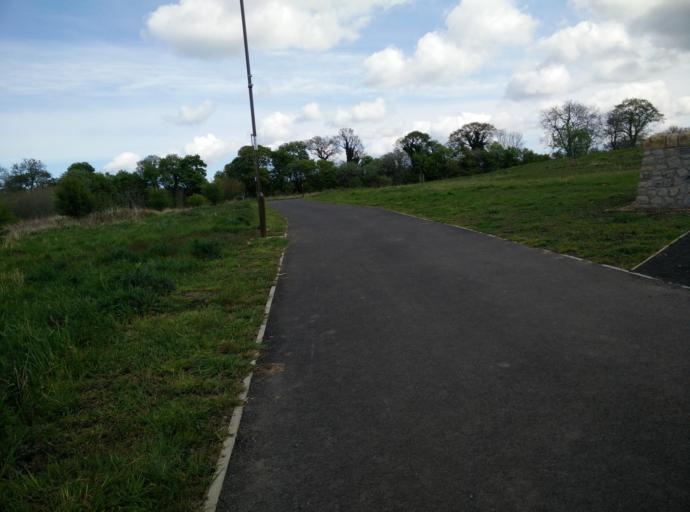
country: GB
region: Scotland
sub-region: Midlothian
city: Bonnyrigg
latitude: 55.9196
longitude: -3.1189
